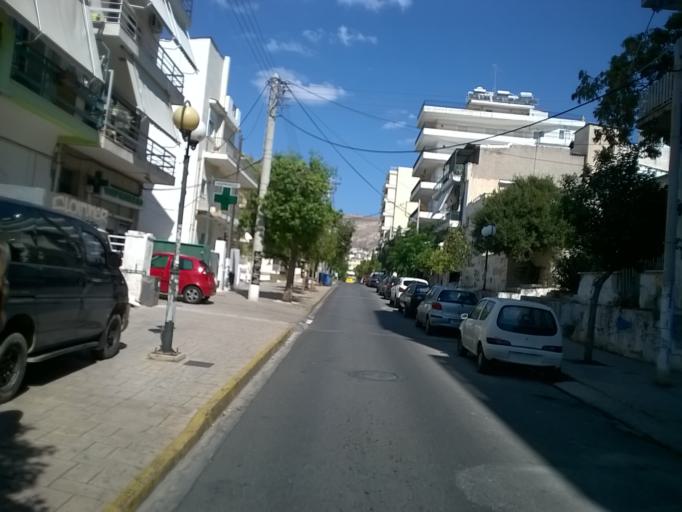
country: GR
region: Attica
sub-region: Nomos Piraios
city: Keratsini
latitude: 37.9674
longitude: 23.6258
